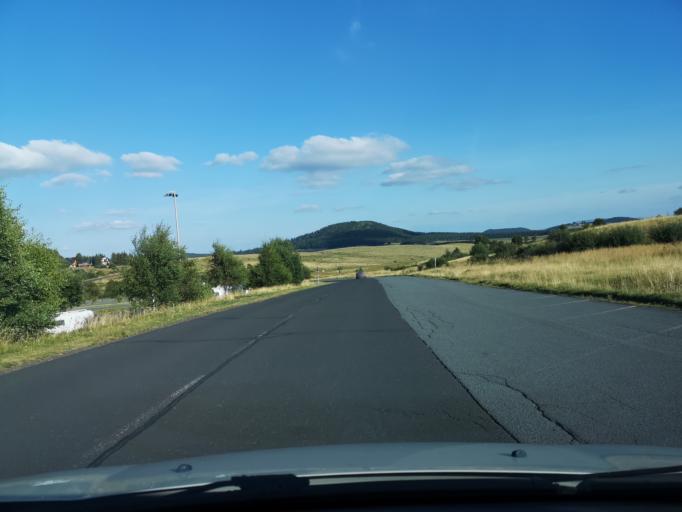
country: FR
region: Auvergne
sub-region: Departement du Puy-de-Dome
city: Mont-Dore
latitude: 45.5039
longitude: 2.8538
